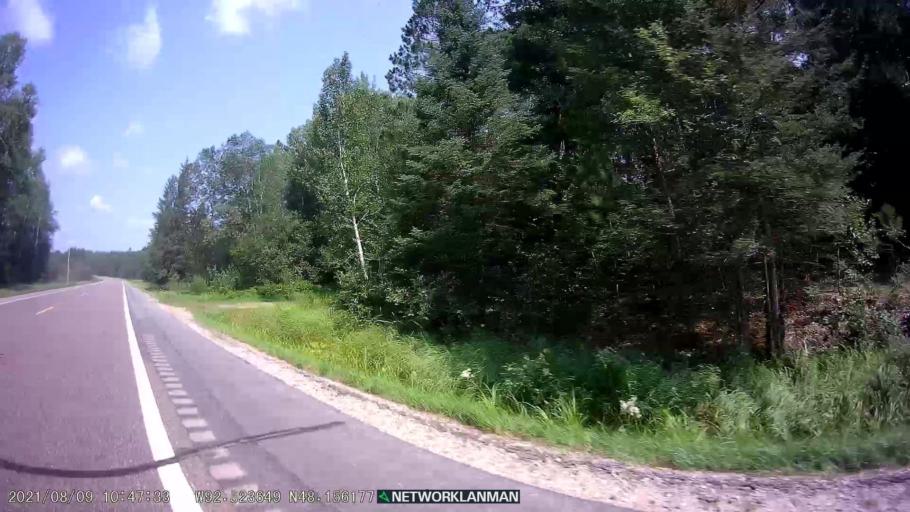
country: US
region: Minnesota
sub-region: Saint Louis County
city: Parkville
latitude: 48.1564
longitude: -92.5237
